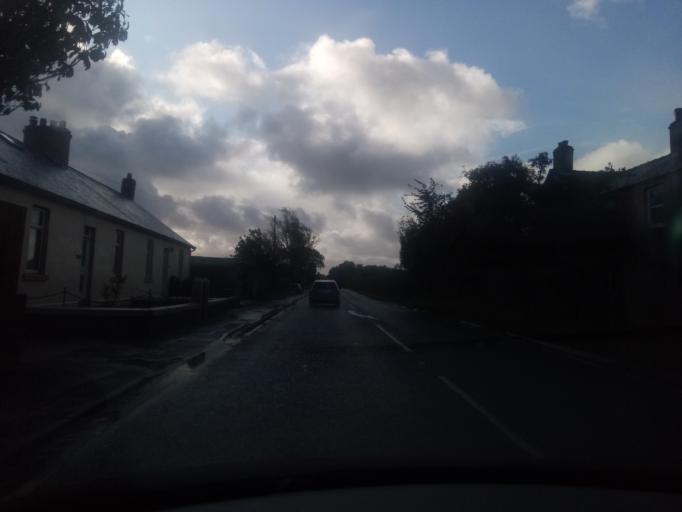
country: GB
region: England
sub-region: Cumbria
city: Carlisle
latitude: 54.9492
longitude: -2.9432
